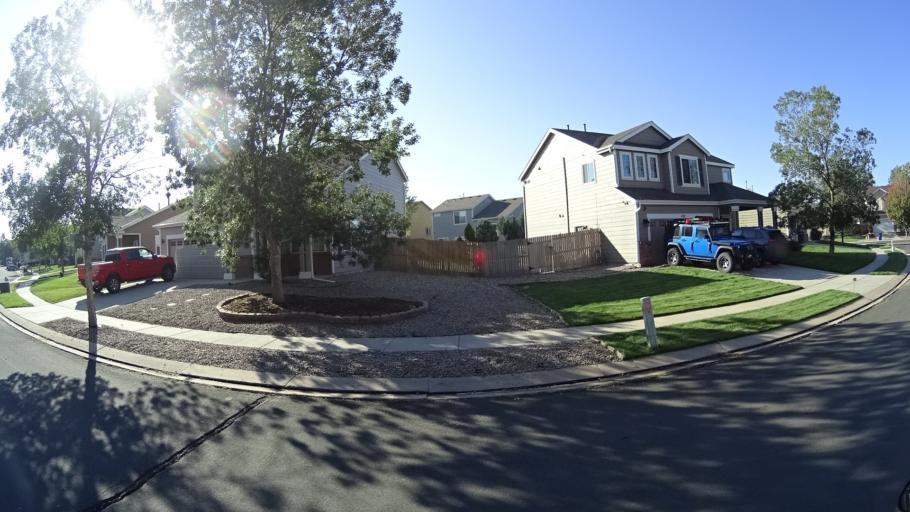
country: US
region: Colorado
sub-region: El Paso County
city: Cimarron Hills
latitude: 38.8837
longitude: -104.6949
